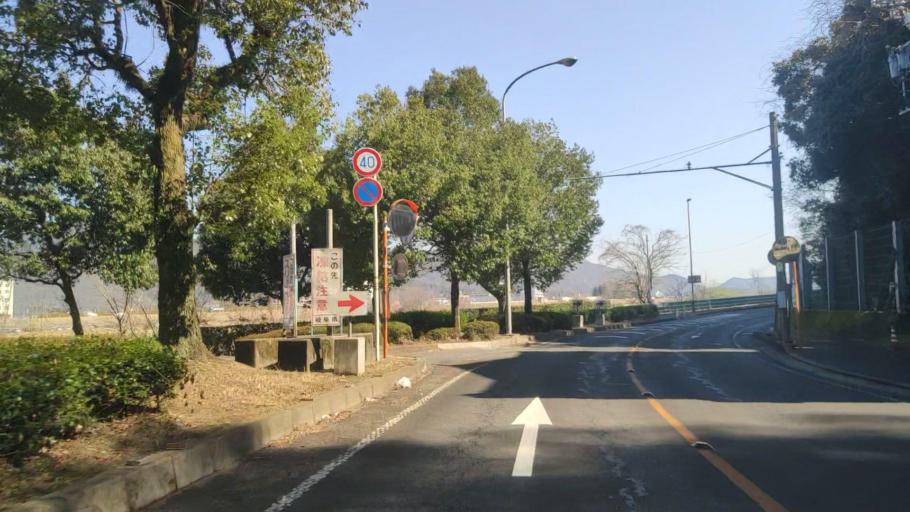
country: JP
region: Gifu
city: Gifu-shi
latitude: 35.4382
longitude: 136.7826
